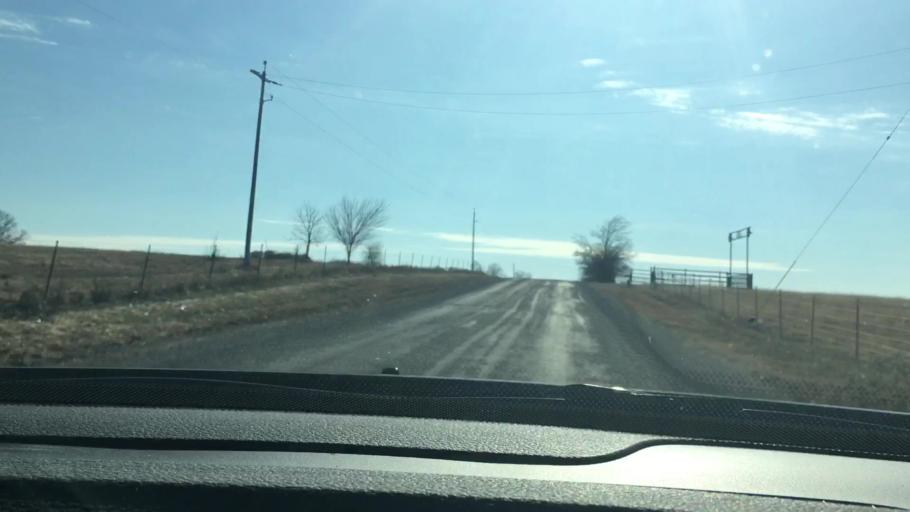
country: US
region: Oklahoma
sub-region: Garvin County
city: Wynnewood
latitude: 34.6580
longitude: -97.0902
